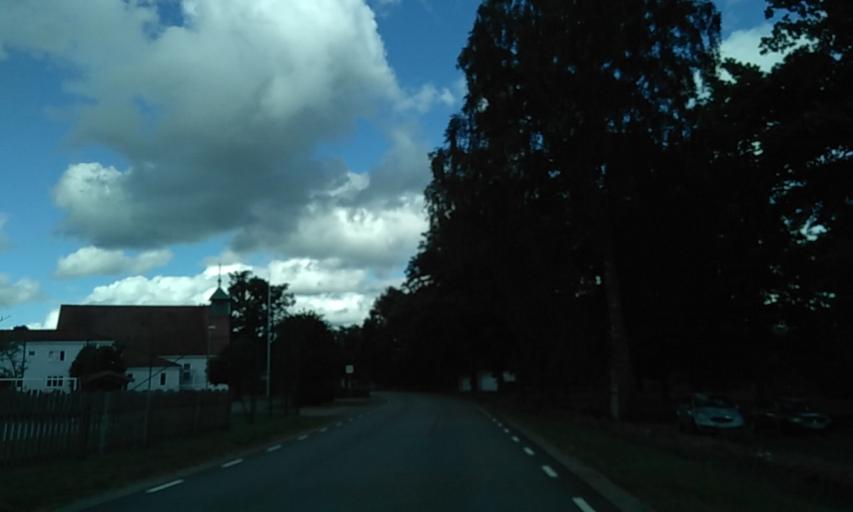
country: SE
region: Vaestra Goetaland
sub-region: Vargarda Kommun
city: Vargarda
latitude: 57.9856
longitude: 12.9254
